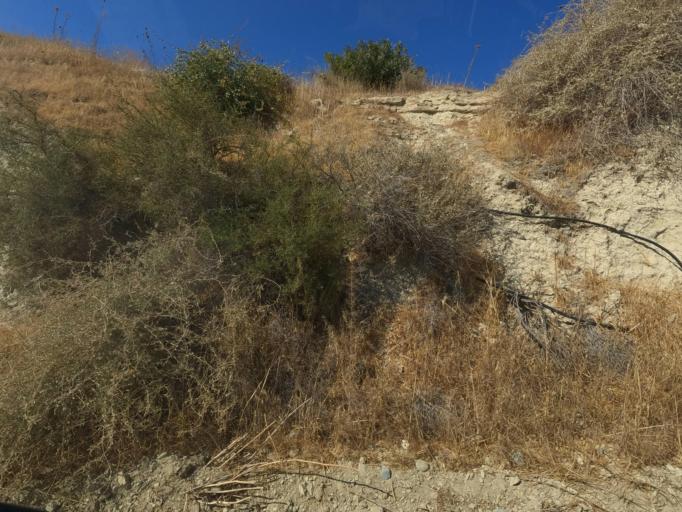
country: CY
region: Pafos
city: Polis
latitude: 34.9904
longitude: 32.4686
